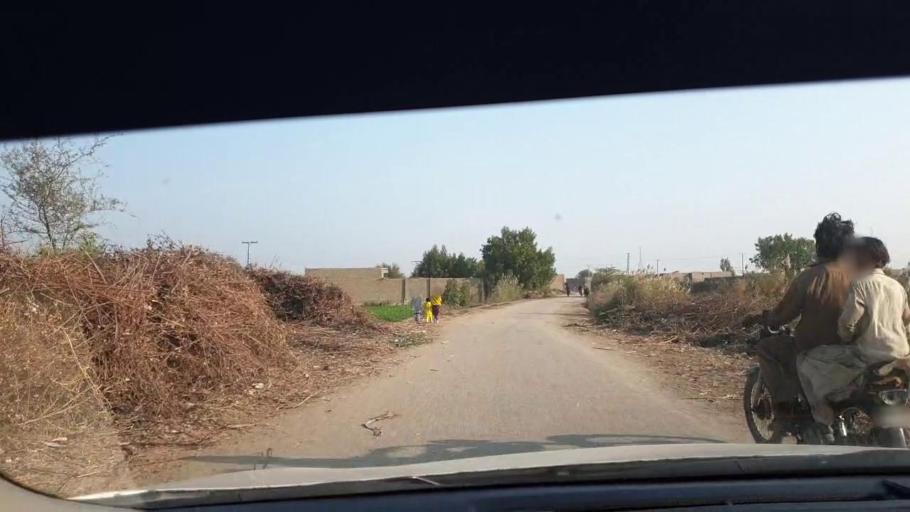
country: PK
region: Sindh
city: Berani
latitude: 25.8427
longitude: 68.7771
